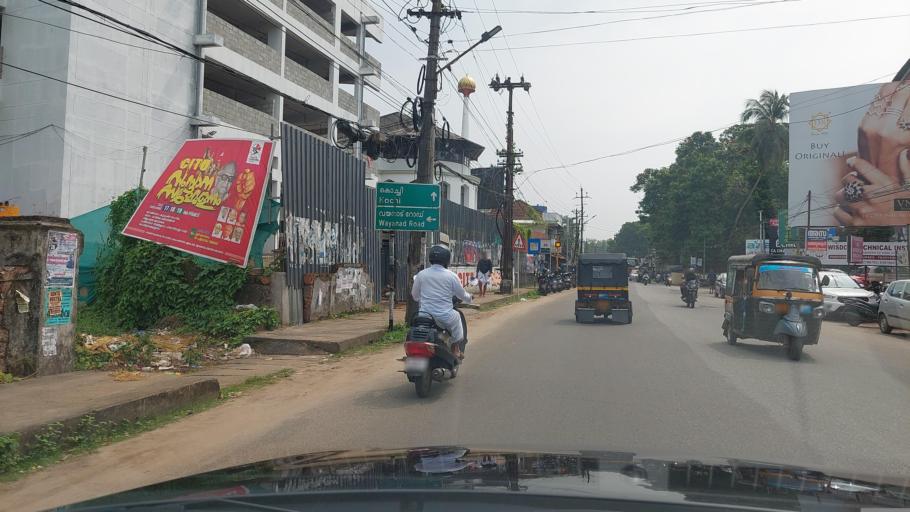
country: IN
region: Kerala
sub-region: Kozhikode
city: Kozhikode
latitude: 11.2726
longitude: 75.7753
